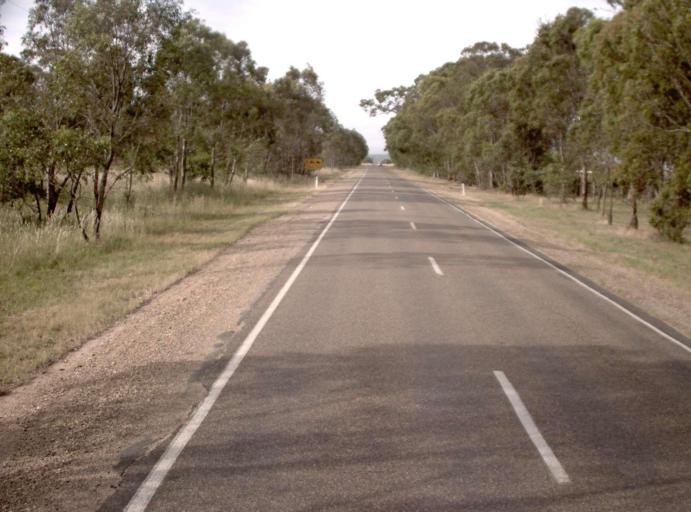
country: AU
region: Victoria
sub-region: Wellington
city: Heyfield
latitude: -38.0310
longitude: 146.6678
